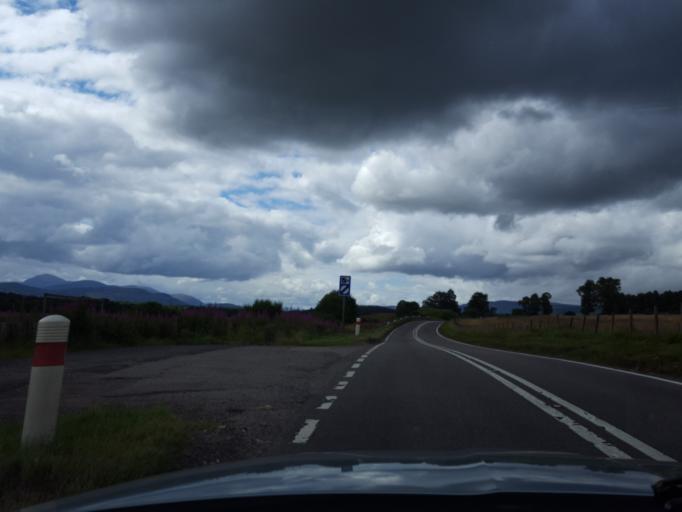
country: GB
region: Scotland
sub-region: Highland
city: Aviemore
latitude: 57.2659
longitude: -3.7287
